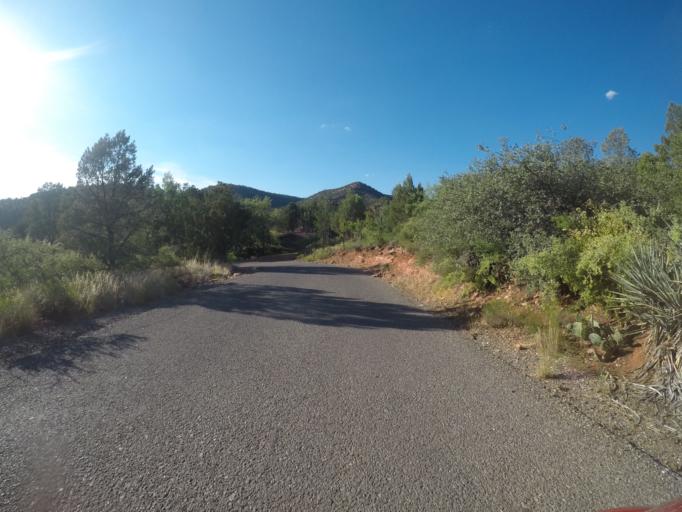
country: US
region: Arizona
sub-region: Yavapai County
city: West Sedona
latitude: 34.8309
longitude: -111.7932
